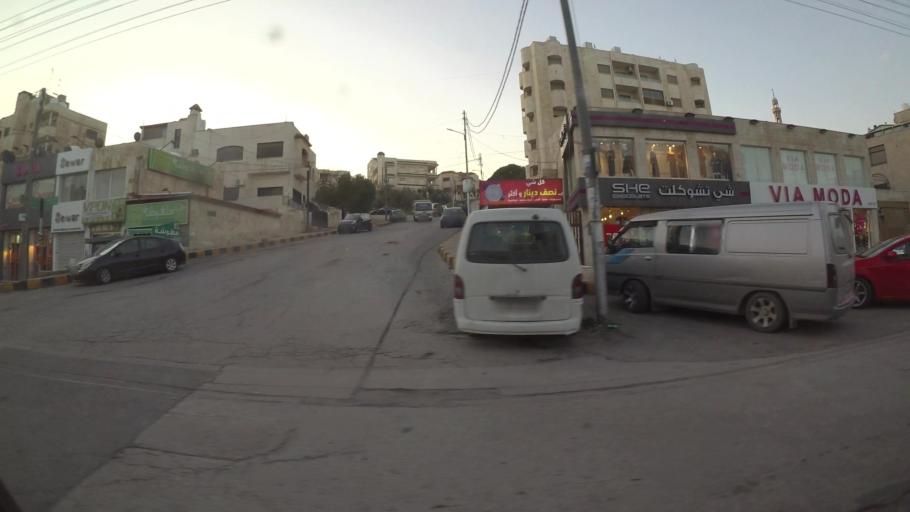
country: JO
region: Amman
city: Al Jubayhah
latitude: 31.9945
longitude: 35.8640
